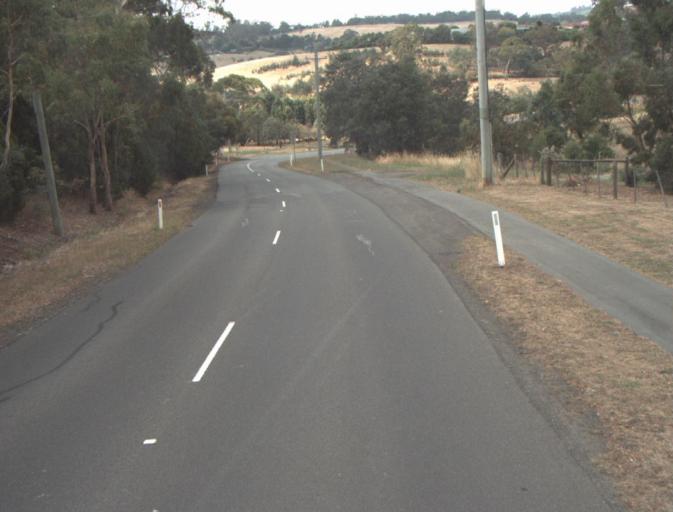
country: AU
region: Tasmania
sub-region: Launceston
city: Newstead
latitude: -41.4722
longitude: 147.1804
